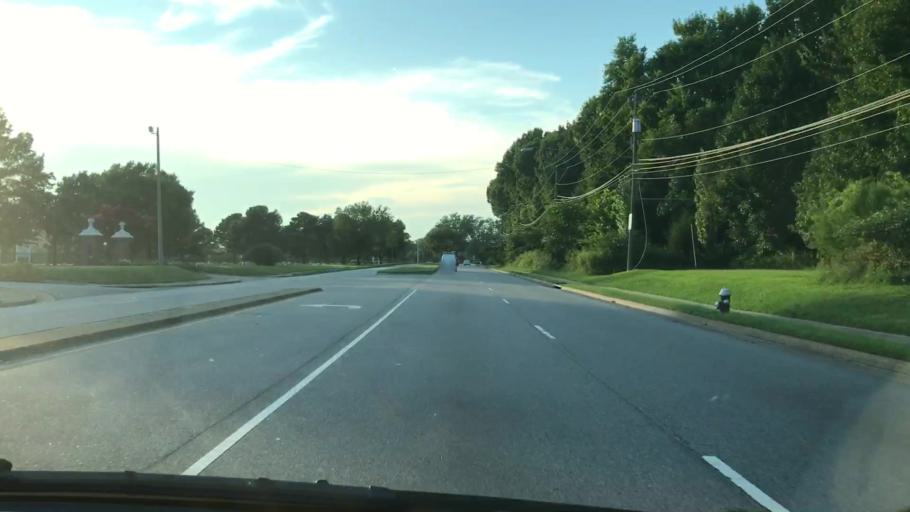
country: US
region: Virginia
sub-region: City of Hampton
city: Hampton
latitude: 37.0558
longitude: -76.3820
